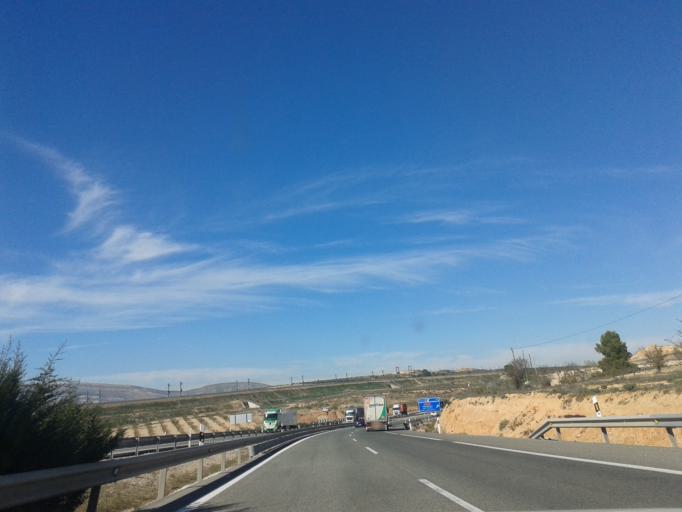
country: ES
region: Castille-La Mancha
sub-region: Provincia de Albacete
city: Caudete
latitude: 38.7060
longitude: -0.9265
